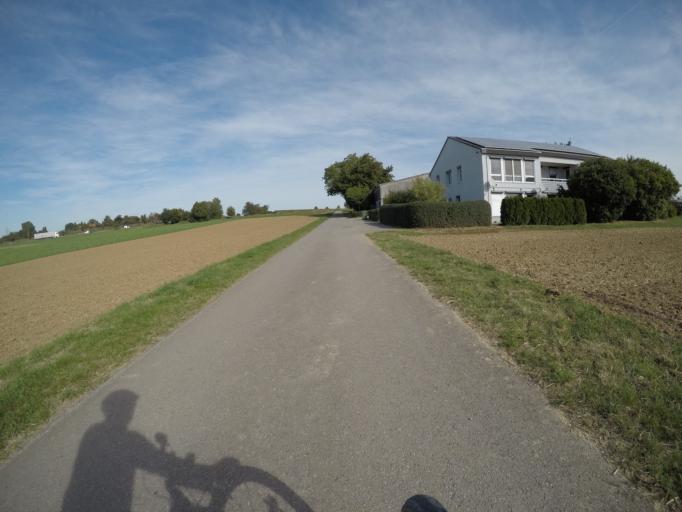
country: DE
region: Baden-Wuerttemberg
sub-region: Regierungsbezirk Stuttgart
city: Moglingen
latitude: 48.8808
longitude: 9.1024
